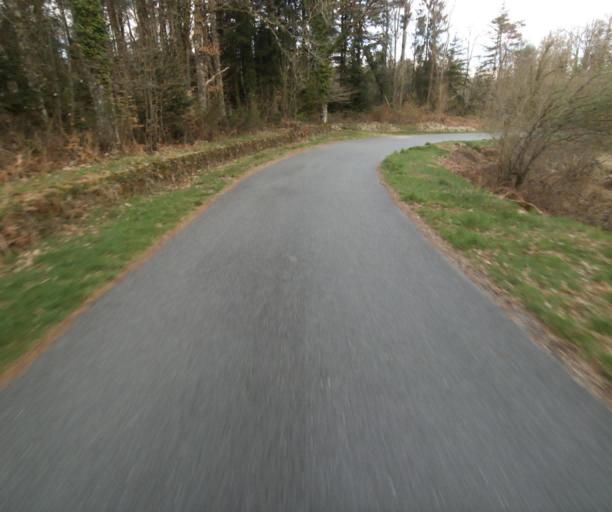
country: FR
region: Limousin
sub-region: Departement de la Correze
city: Correze
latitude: 45.2467
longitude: 1.9580
